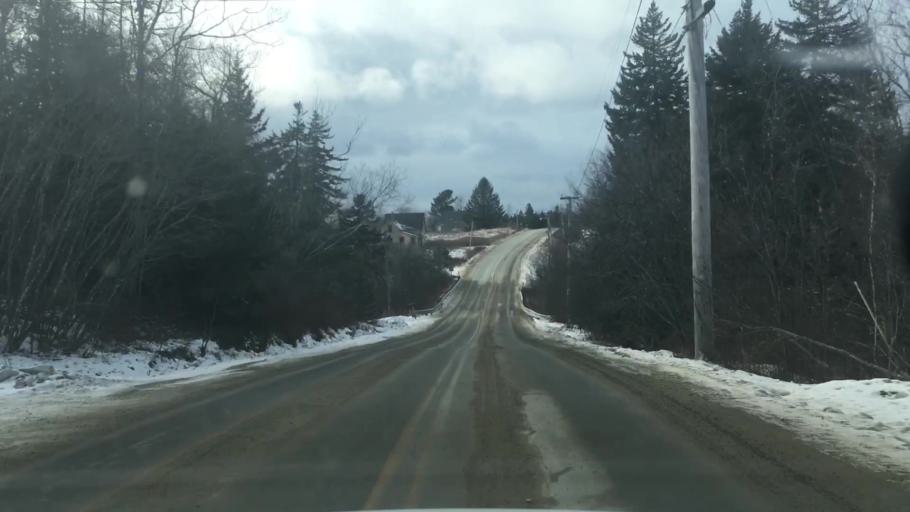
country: US
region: Maine
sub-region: Washington County
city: Machias
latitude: 44.6633
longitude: -67.5515
